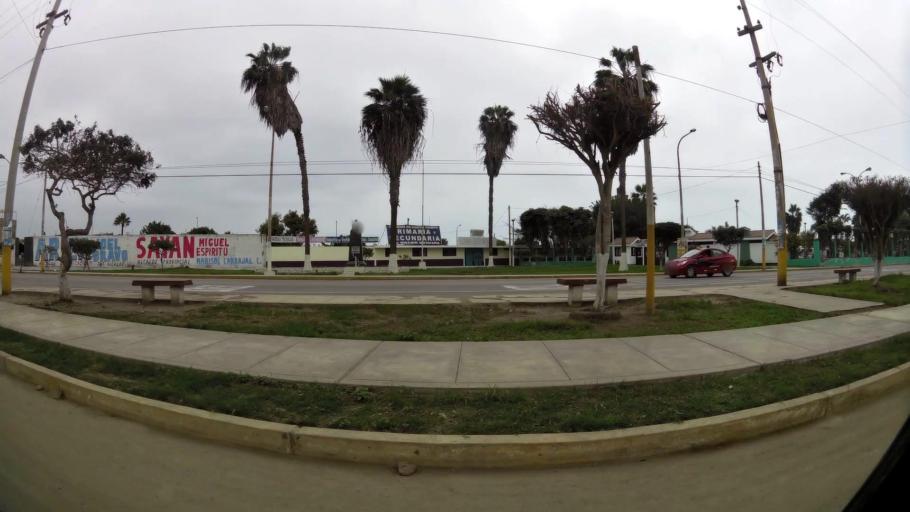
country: PE
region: Lima
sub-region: Barranca
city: Paramonga
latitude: -10.6742
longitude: -77.8140
